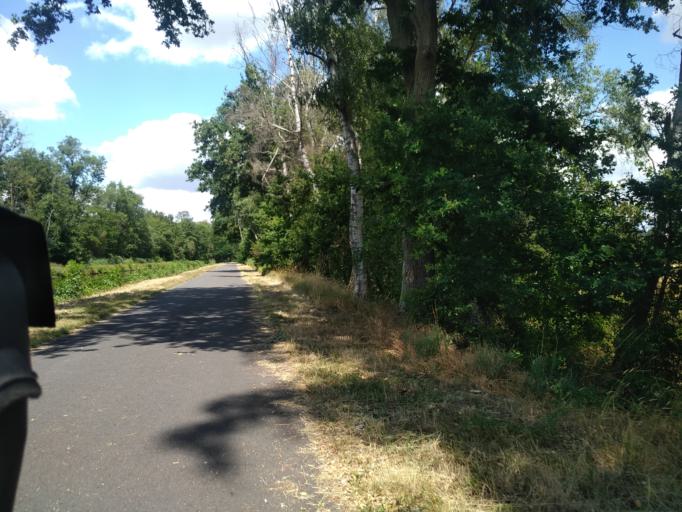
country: FR
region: Rhone-Alpes
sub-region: Departement de la Loire
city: Briennon
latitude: 46.1233
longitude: 4.0767
